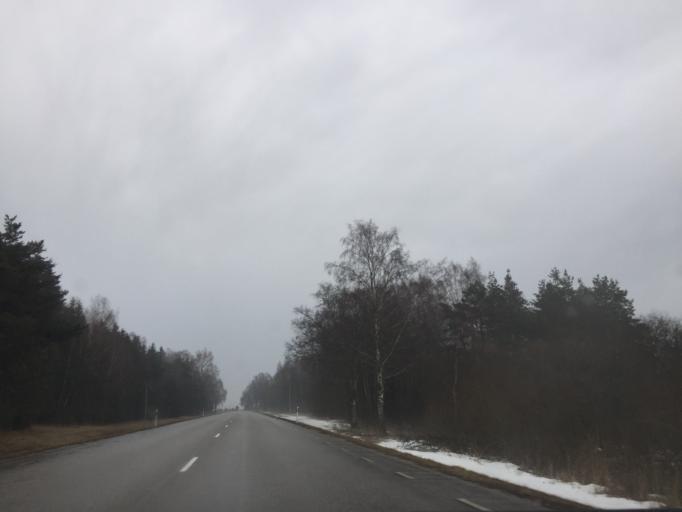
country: EE
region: Saare
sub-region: Orissaare vald
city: Orissaare
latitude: 58.5500
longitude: 23.1183
